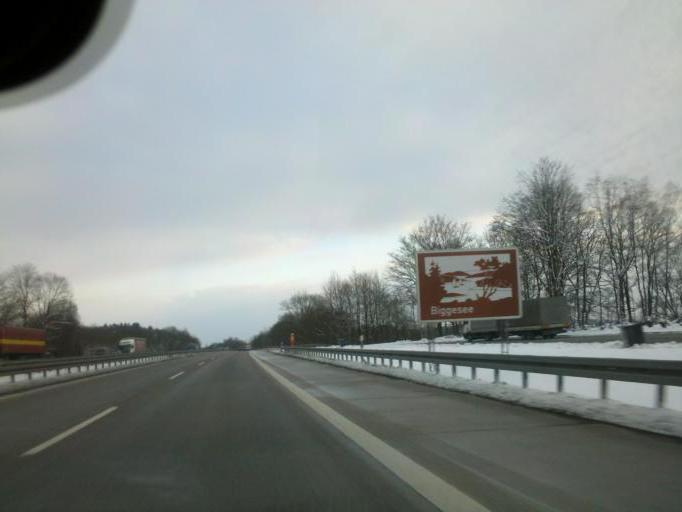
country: DE
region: North Rhine-Westphalia
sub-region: Regierungsbezirk Arnsberg
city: Drolshagen
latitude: 51.0455
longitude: 7.7967
